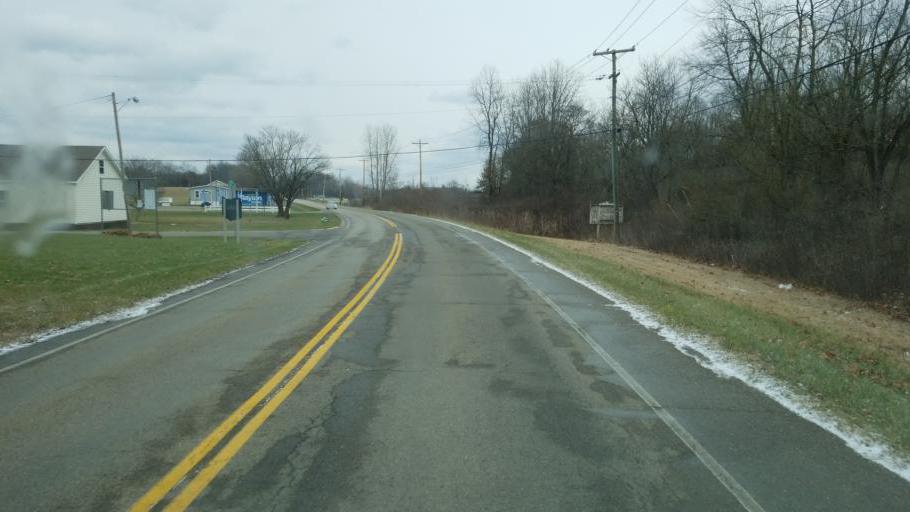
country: US
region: Ohio
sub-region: Muskingum County
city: Frazeysburg
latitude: 40.1196
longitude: -82.1106
